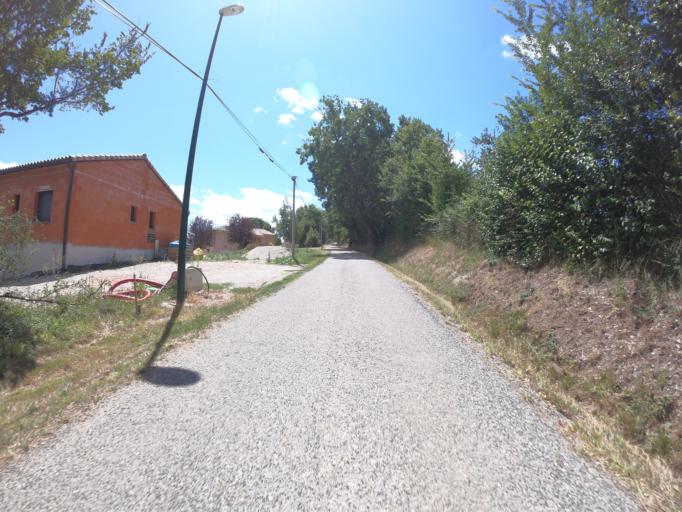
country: FR
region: Midi-Pyrenees
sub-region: Departement de l'Ariege
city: La Tour-du-Crieu
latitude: 43.0793
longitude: 1.7375
